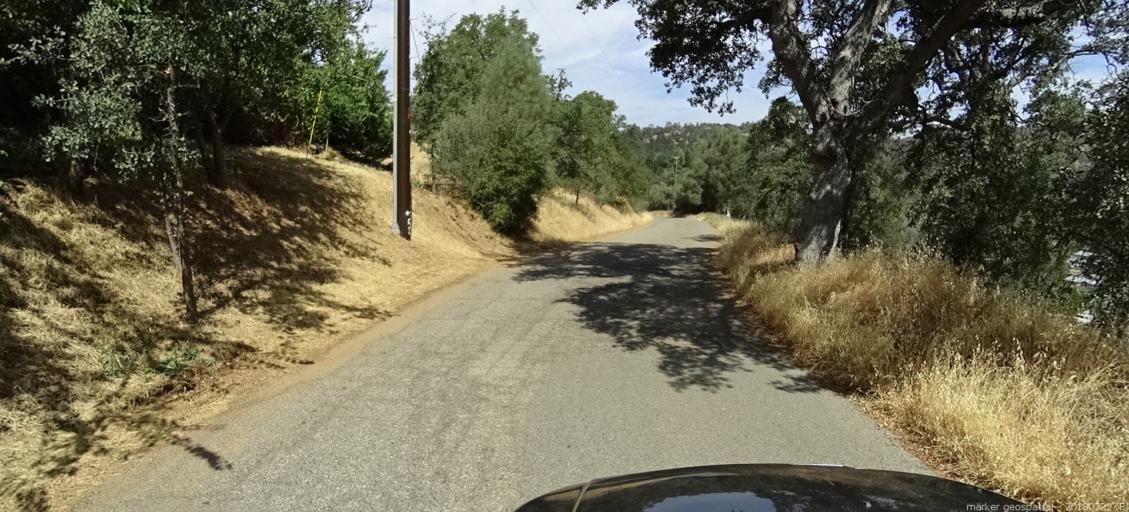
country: US
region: California
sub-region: Madera County
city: Coarsegold
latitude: 37.2613
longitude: -119.7077
